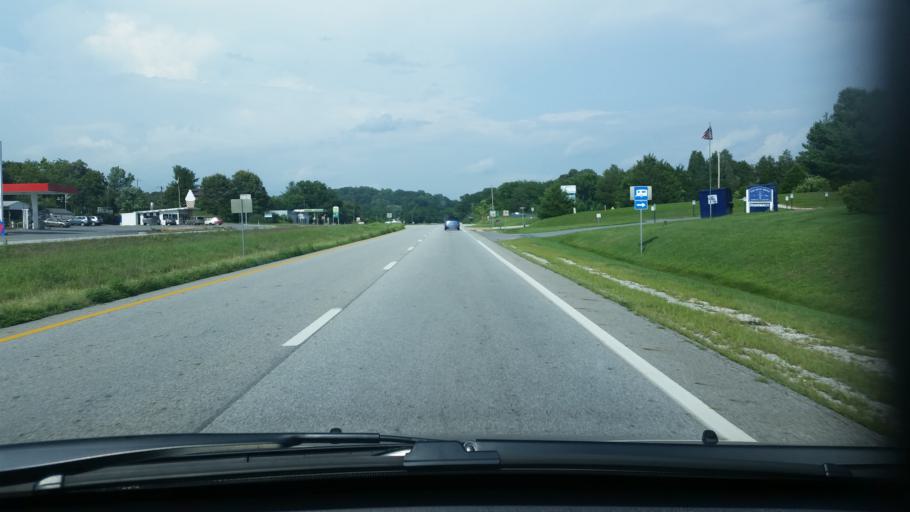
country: US
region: Virginia
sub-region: Nelson County
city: Lovingston
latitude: 37.7073
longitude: -78.9346
